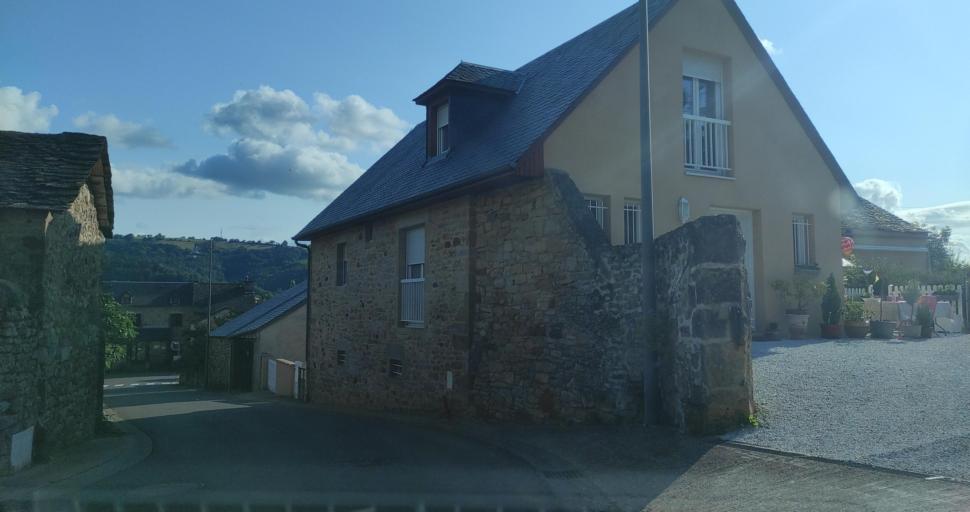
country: FR
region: Midi-Pyrenees
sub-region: Departement de l'Aveyron
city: La Loubiere
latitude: 44.3595
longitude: 2.6808
